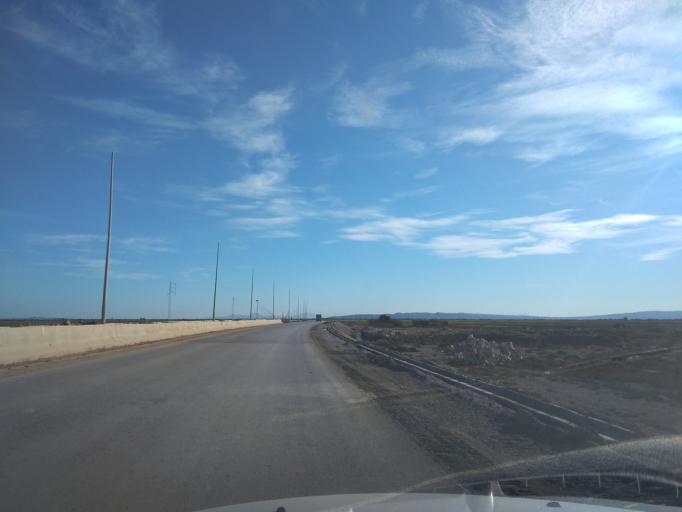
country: TN
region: Ariana
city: Qal'at al Andalus
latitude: 37.0388
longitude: 10.1322
